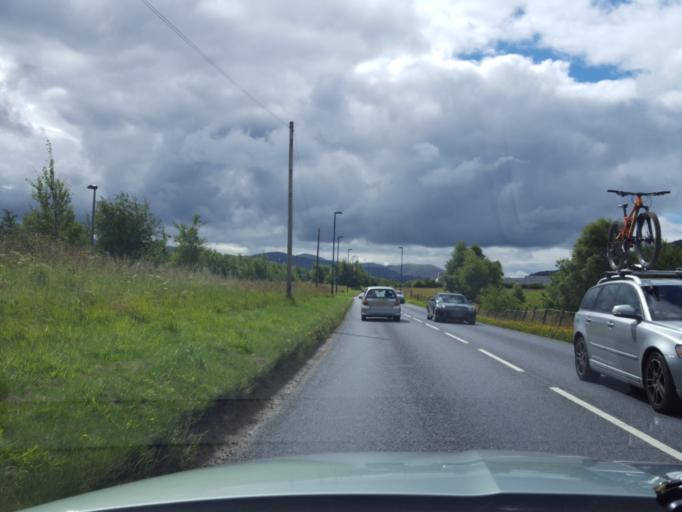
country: GB
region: Scotland
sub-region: Highland
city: Aviemore
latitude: 57.2058
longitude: -3.8267
